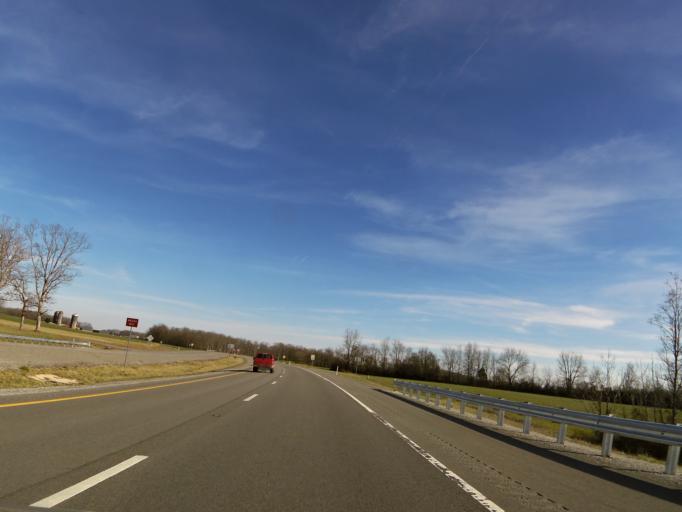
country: US
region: Tennessee
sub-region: Cannon County
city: Woodbury
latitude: 35.7664
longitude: -85.9737
